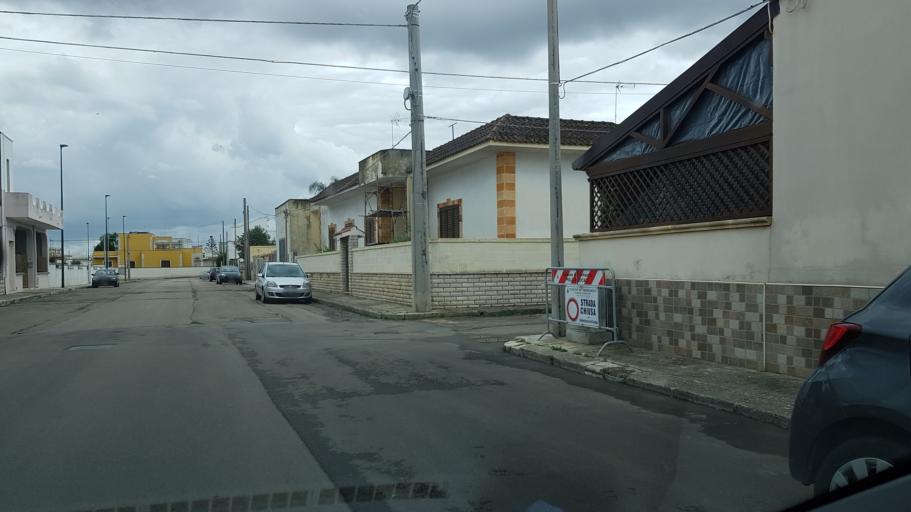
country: IT
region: Apulia
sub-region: Provincia di Brindisi
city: Torchiarolo
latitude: 40.4875
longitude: 18.0543
